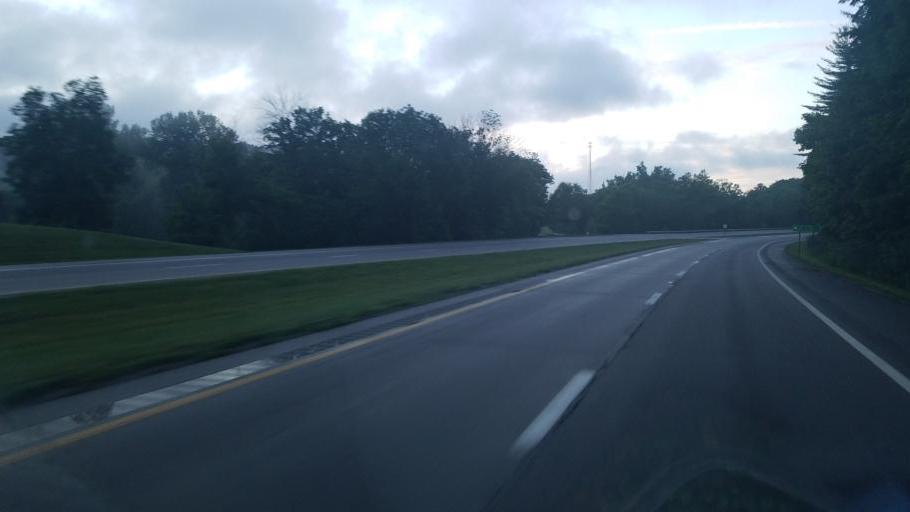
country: US
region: Ohio
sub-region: Jackson County
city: Jackson
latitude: 39.1905
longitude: -82.7686
